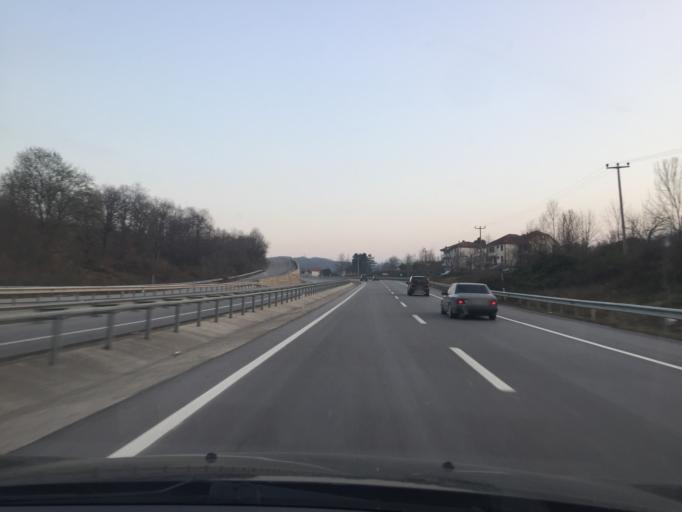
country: TR
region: Sakarya
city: Akyazi
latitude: 40.6288
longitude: 30.6424
